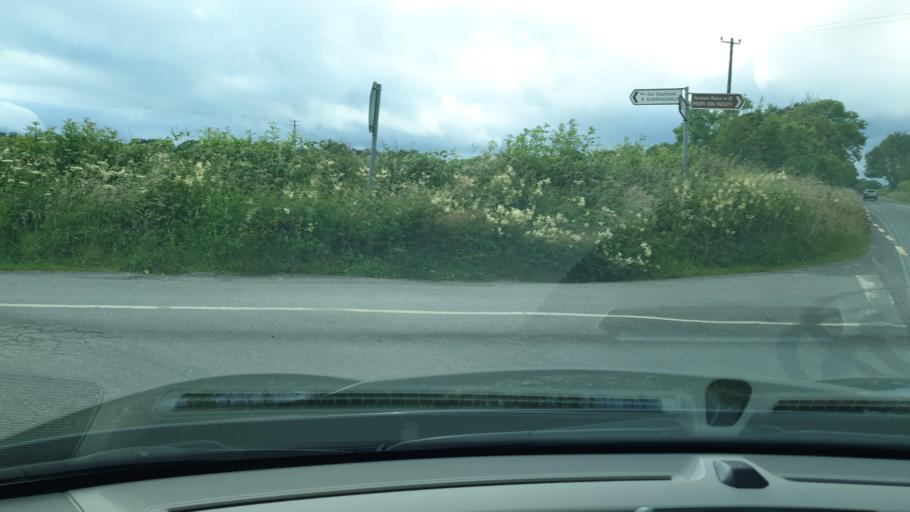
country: IE
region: Leinster
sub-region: An Mhi
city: Dunshaughlin
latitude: 53.5414
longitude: -6.5068
